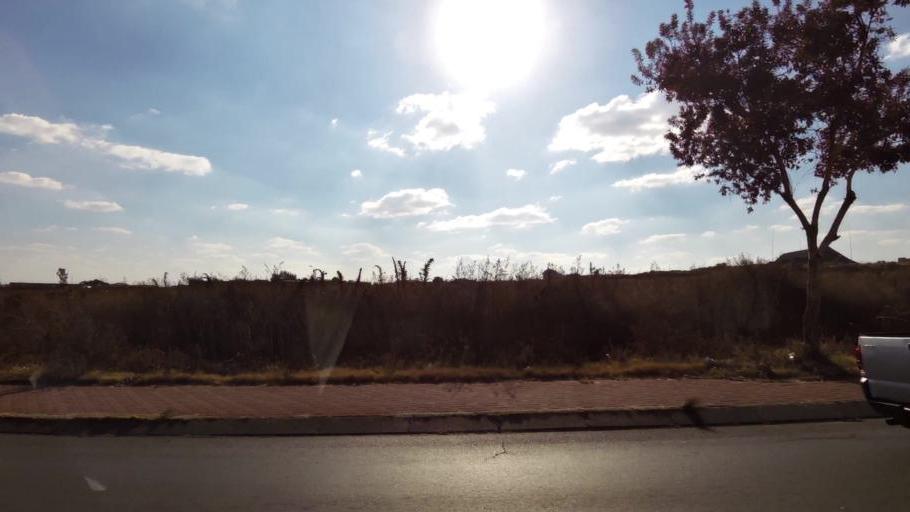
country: ZA
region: Gauteng
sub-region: City of Johannesburg Metropolitan Municipality
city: Soweto
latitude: -26.2240
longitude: 27.8872
